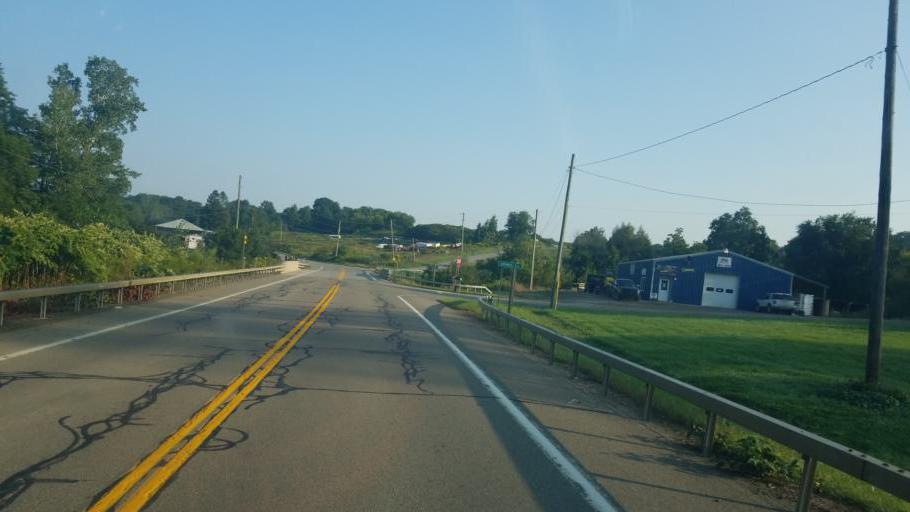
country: US
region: Pennsylvania
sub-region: Tioga County
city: Westfield
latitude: 42.0172
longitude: -77.5214
